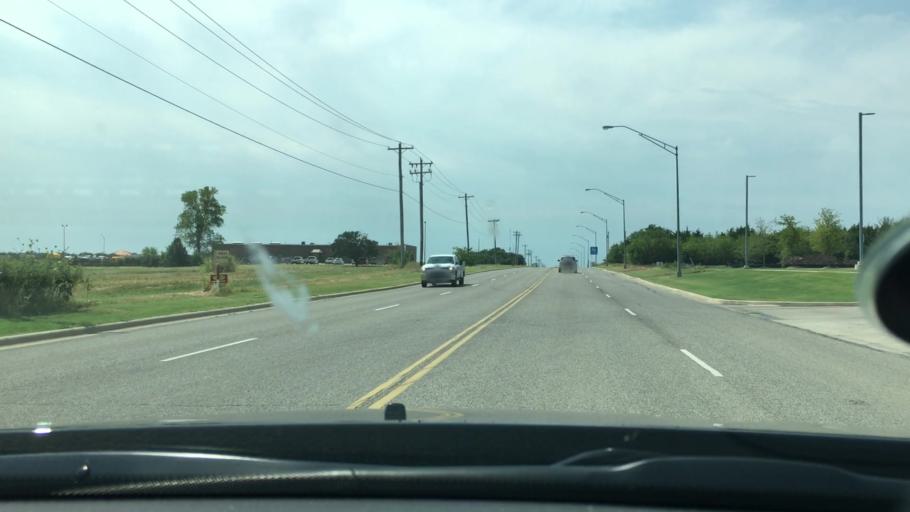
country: US
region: Oklahoma
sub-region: Carter County
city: Ardmore
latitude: 34.1973
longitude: -97.1605
